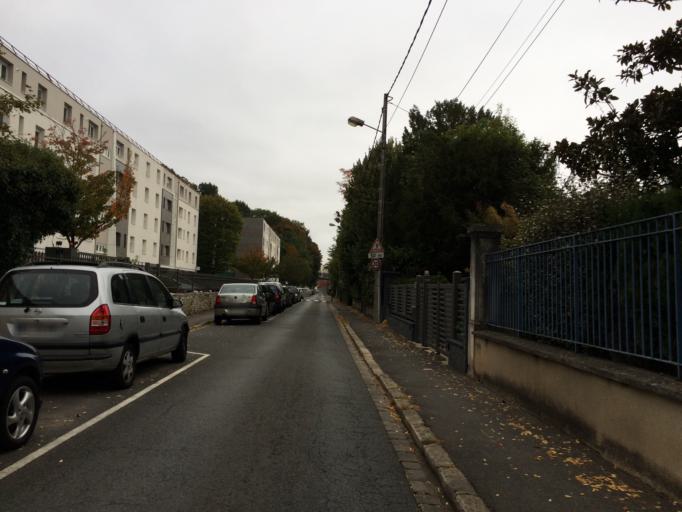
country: FR
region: Ile-de-France
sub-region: Departement de l'Essonne
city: Orsay
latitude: 48.6989
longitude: 2.1964
